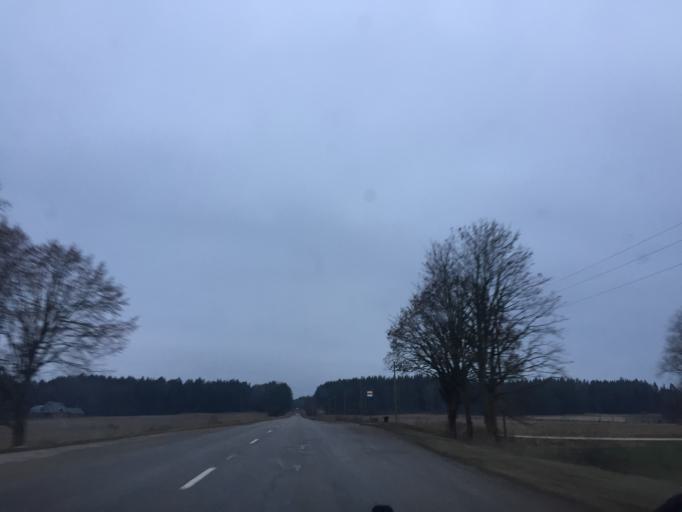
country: LV
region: Priekuli
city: Priekuli
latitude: 57.3237
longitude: 25.4396
